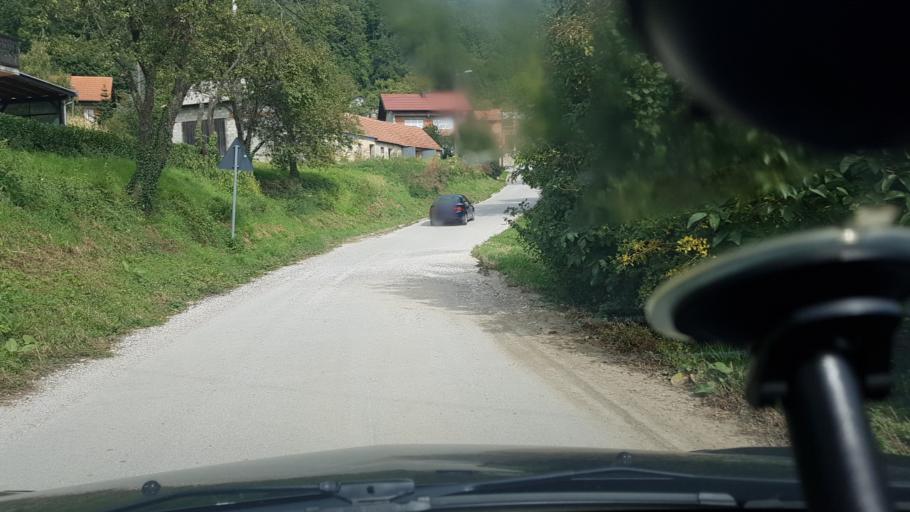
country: HR
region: Varazdinska
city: Ljubescica
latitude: 46.1277
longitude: 16.4618
